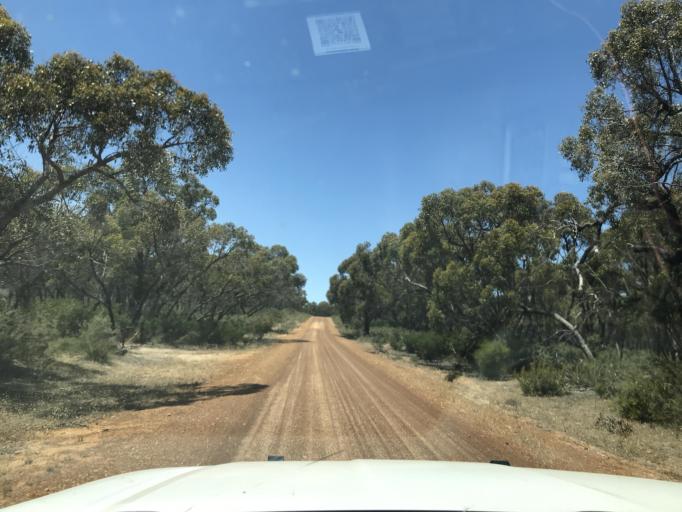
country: AU
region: South Australia
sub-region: Wattle Range
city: Penola
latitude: -37.0465
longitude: 141.3937
